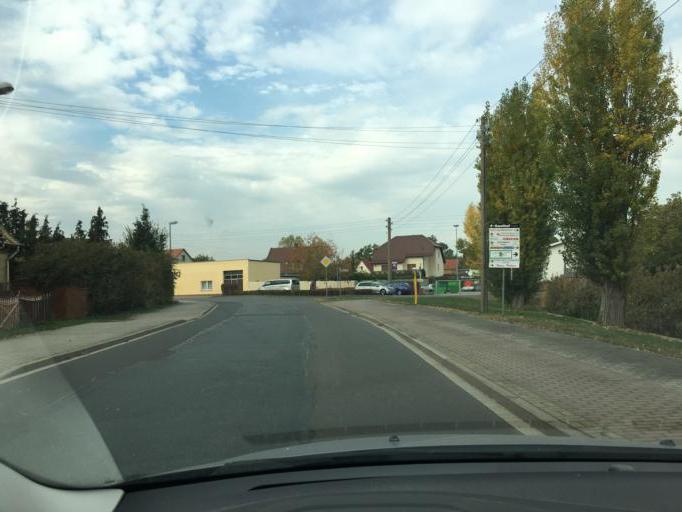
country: DE
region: Saxony
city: Zwochau
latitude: 51.4224
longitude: 12.2986
